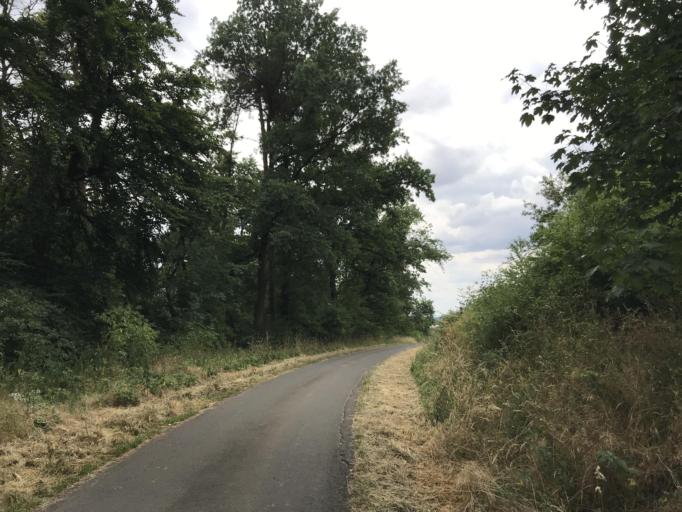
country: DE
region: Hesse
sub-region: Regierungsbezirk Giessen
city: Grunberg
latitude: 50.5858
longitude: 8.9375
